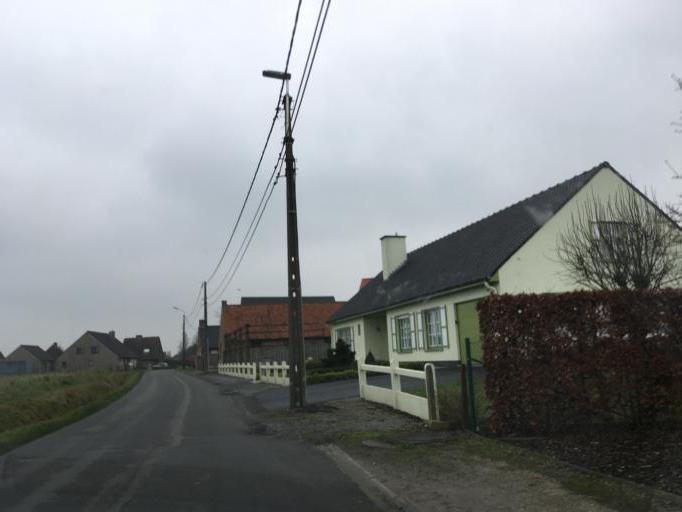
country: BE
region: Flanders
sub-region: Provincie West-Vlaanderen
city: Roeselare
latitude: 50.9751
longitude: 3.1374
